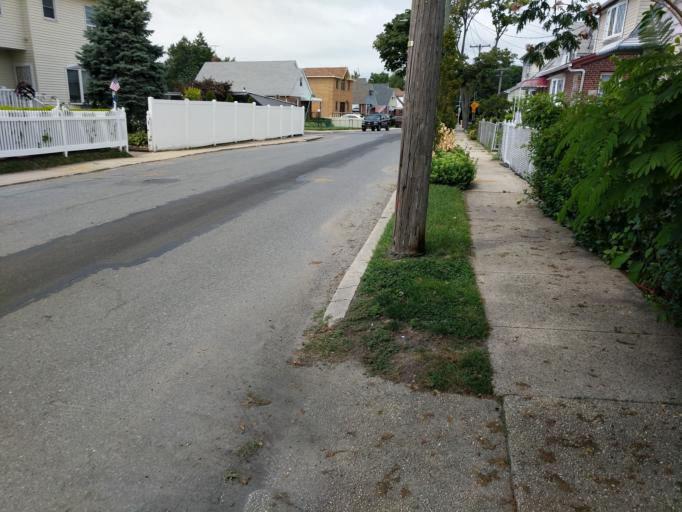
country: US
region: New York
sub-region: Nassau County
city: Valley Stream
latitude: 40.6783
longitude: -73.7277
